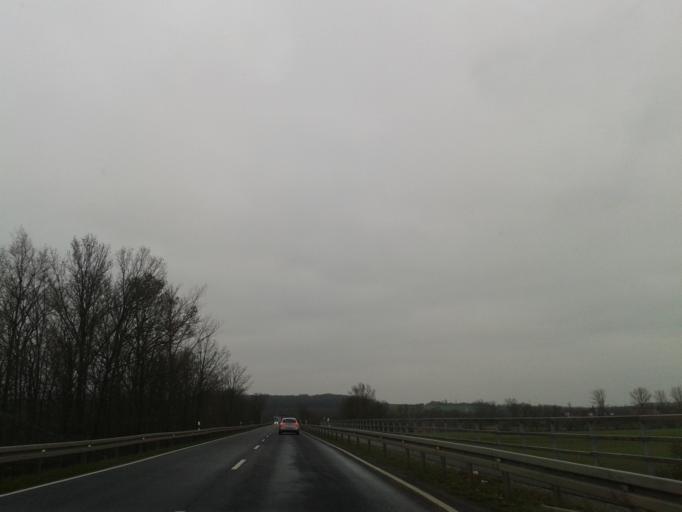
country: DE
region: Bavaria
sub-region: Regierungsbezirk Unterfranken
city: Wonfurt
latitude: 50.0140
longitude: 10.4339
